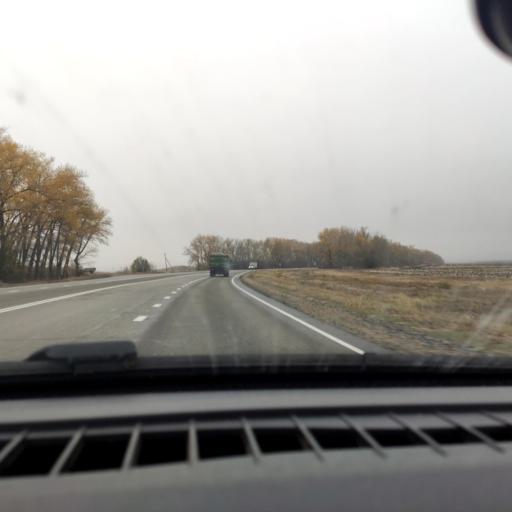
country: RU
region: Voronezj
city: Ostrogozhsk
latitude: 50.9753
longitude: 38.9941
